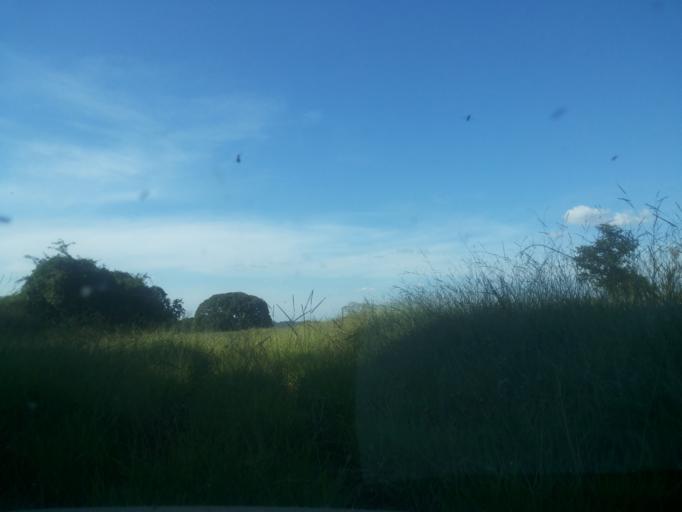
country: BR
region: Minas Gerais
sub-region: Santa Vitoria
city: Santa Vitoria
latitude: -19.0009
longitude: -50.4482
